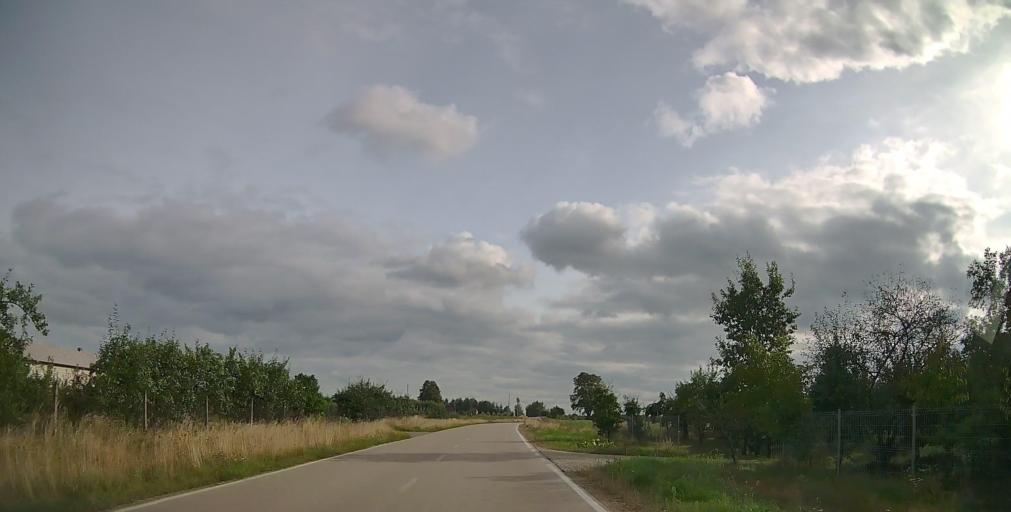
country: PL
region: Masovian Voivodeship
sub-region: Powiat grojecki
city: Goszczyn
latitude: 51.7581
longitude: 20.9015
